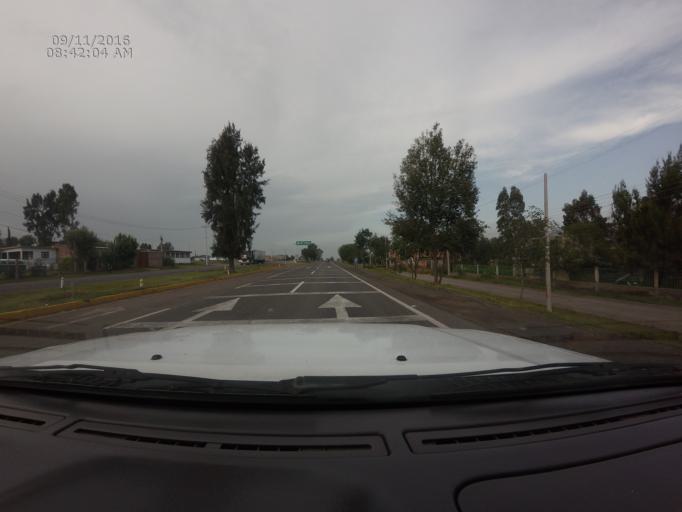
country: MX
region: Michoacan
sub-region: Morelia
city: La Mintzita (Piedra Dura)
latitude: 19.5941
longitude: -101.2963
